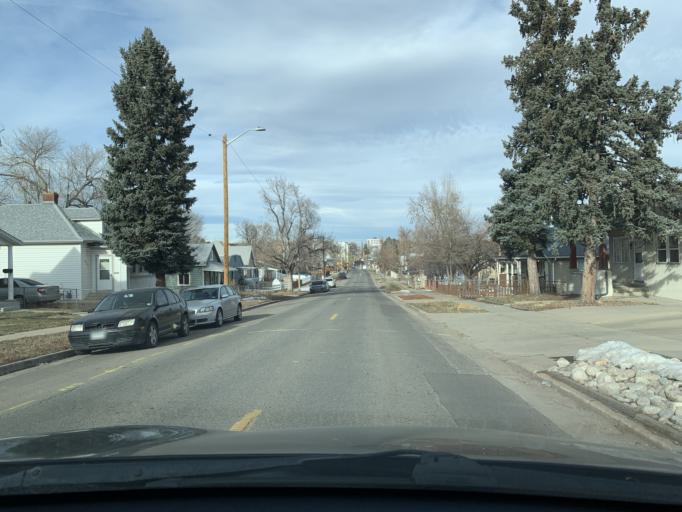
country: US
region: Colorado
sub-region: Jefferson County
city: Edgewater
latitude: 39.7314
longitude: -105.0321
